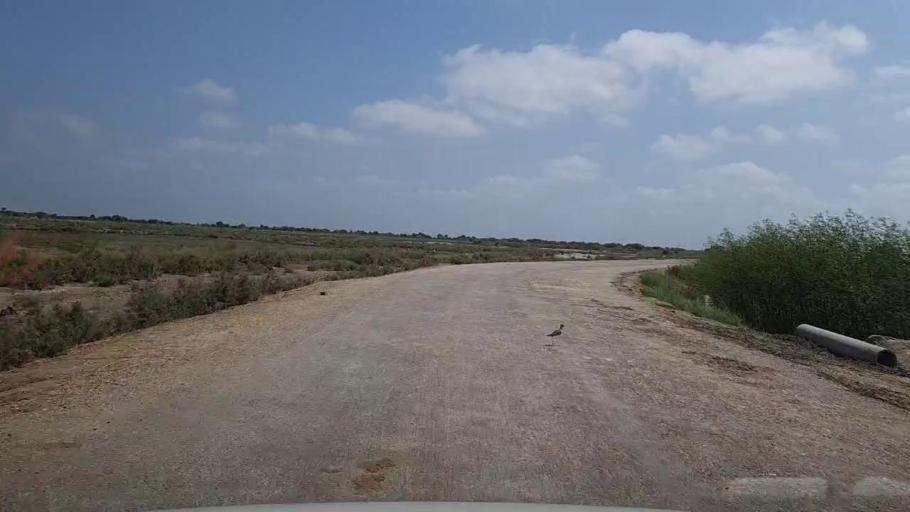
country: PK
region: Sindh
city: Talhar
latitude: 24.8810
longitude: 68.7158
